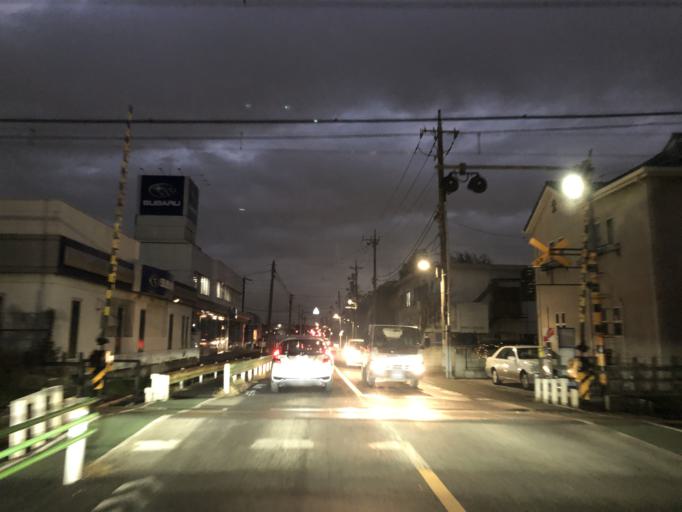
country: JP
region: Tokyo
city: Kokubunji
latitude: 35.7170
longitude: 139.4601
